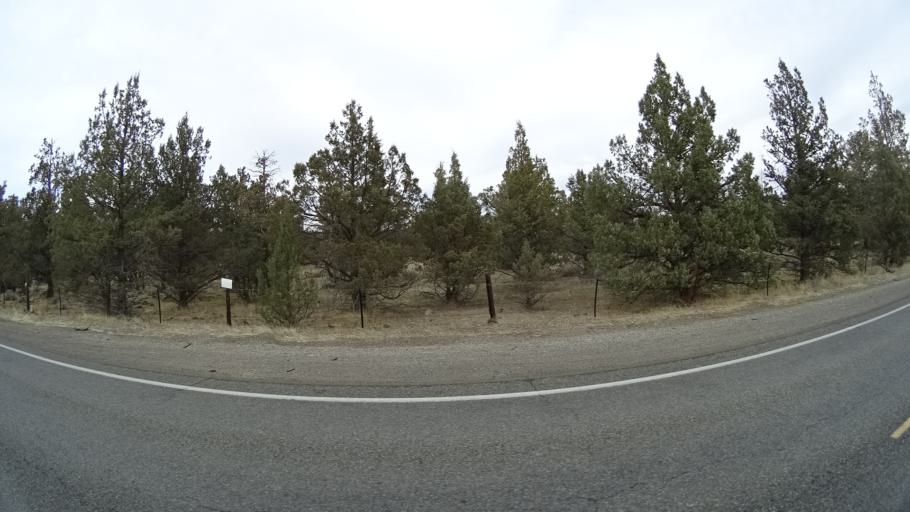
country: US
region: California
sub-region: Siskiyou County
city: Montague
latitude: 41.6347
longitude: -122.4438
